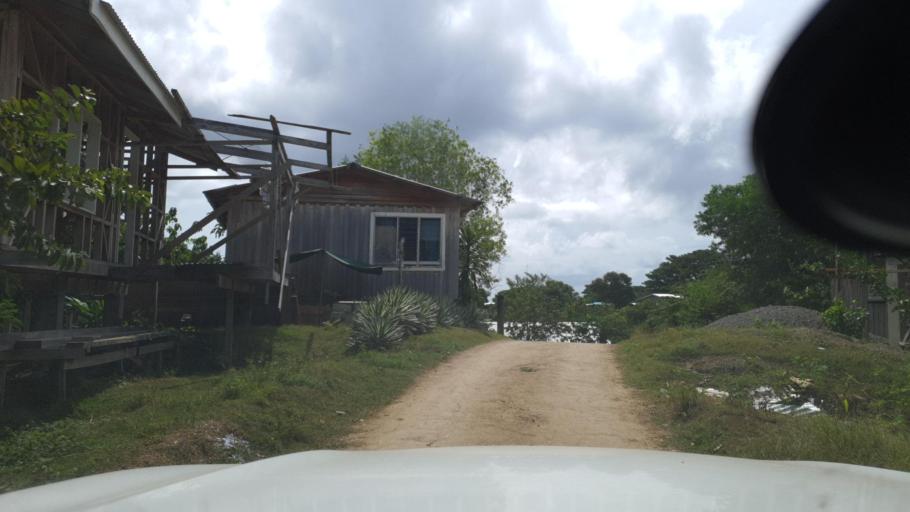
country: SB
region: Guadalcanal
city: Honiara
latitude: -9.4308
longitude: 159.9295
